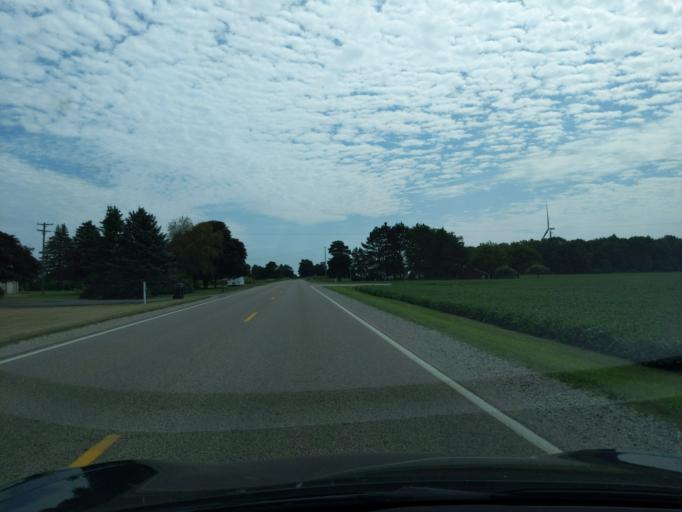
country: US
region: Michigan
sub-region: Gratiot County
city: Ithaca
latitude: 43.2916
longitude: -84.5248
